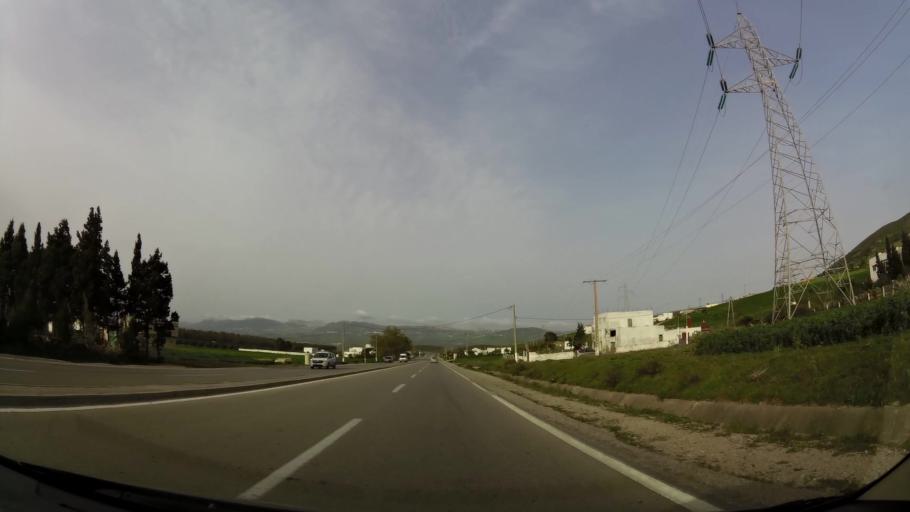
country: MA
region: Tanger-Tetouan
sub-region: Tetouan
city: Saddina
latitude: 35.5551
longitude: -5.5056
